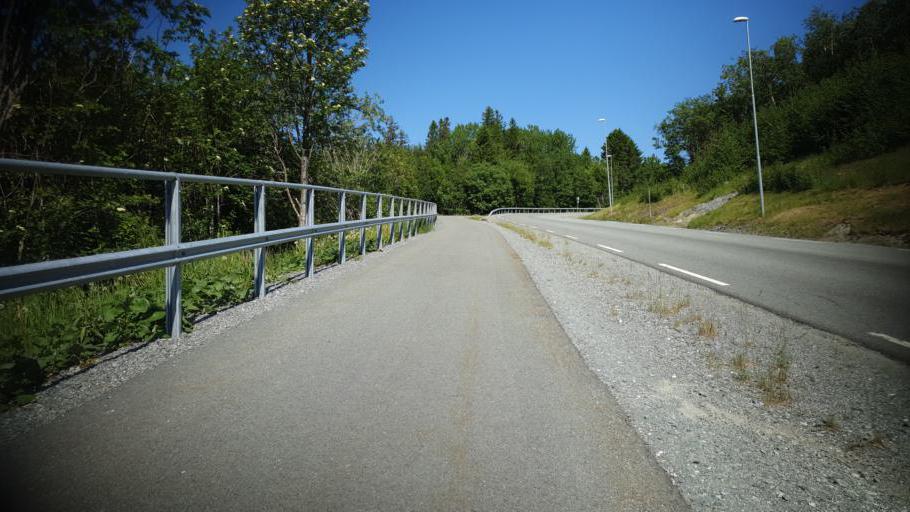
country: NO
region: Sor-Trondelag
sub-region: Malvik
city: Malvik
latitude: 63.4316
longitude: 10.5887
